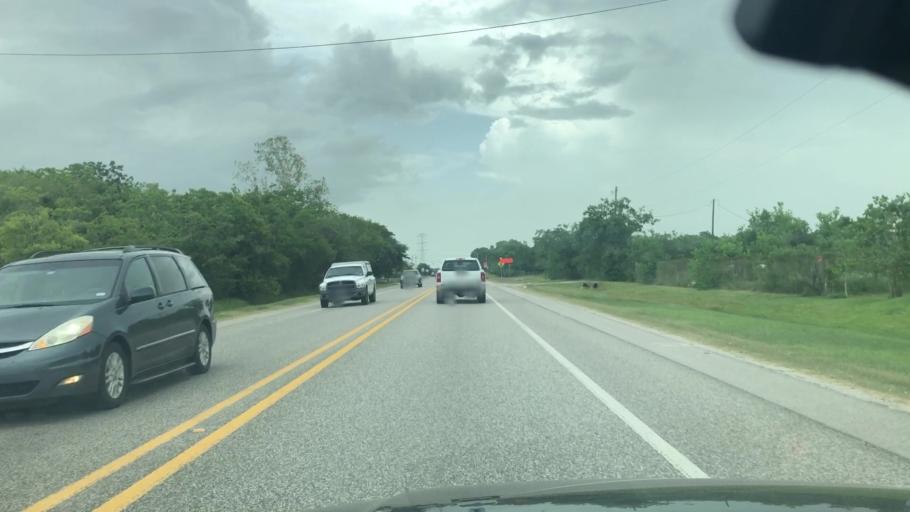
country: US
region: Texas
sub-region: Galveston County
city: Dickinson
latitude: 29.4857
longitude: -95.0624
